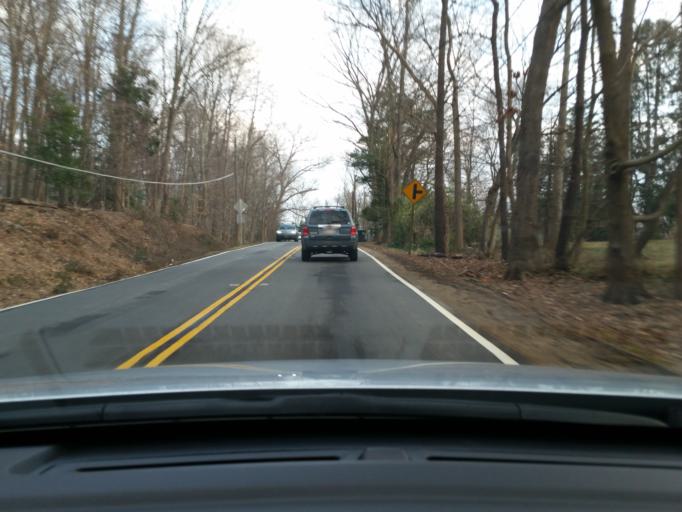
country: US
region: Virginia
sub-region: Fairfax County
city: Great Falls
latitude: 38.9726
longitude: -77.2425
